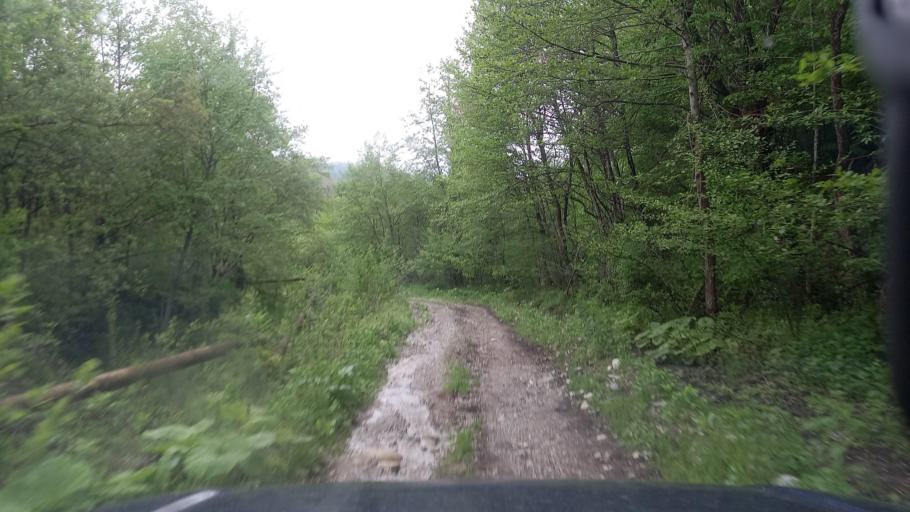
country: RU
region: Kabardino-Balkariya
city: Kashkhatau
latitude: 43.2988
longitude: 43.5895
